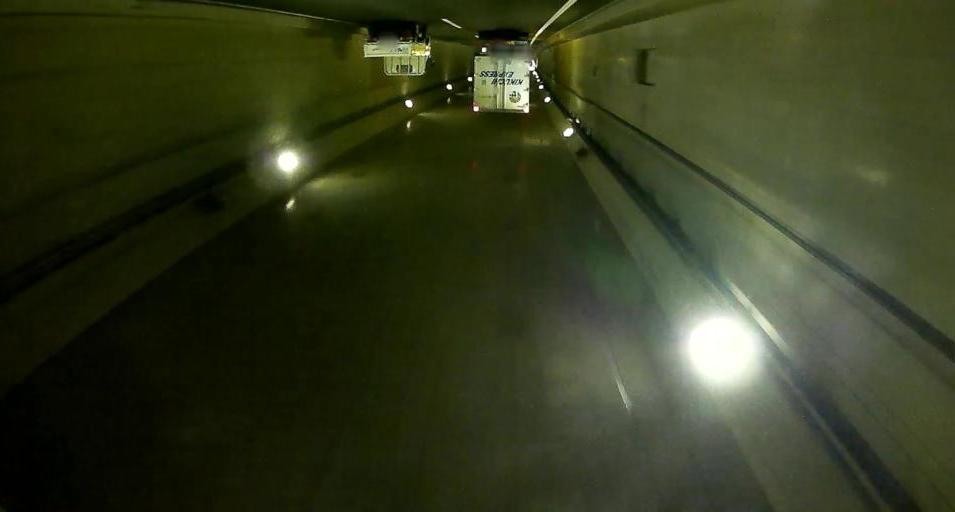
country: JP
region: Chiba
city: Chiba
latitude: 35.6102
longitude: 140.1062
